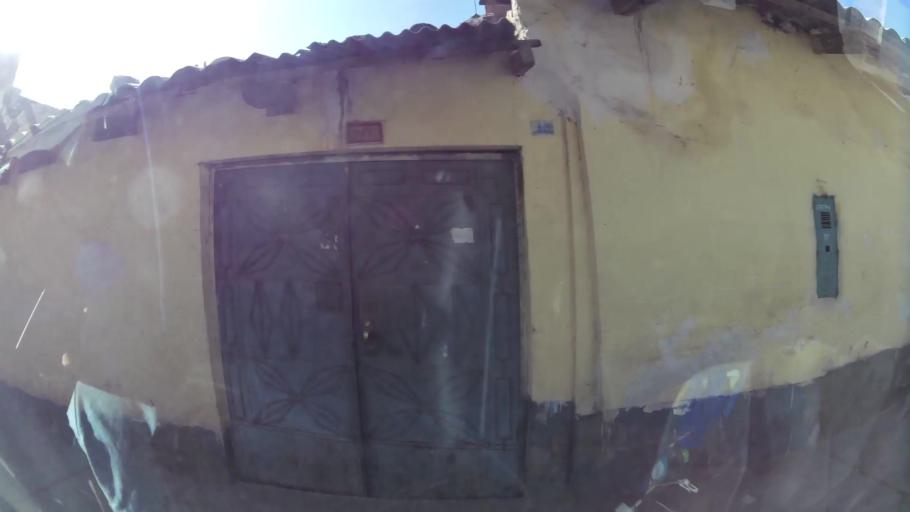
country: PE
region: Ayacucho
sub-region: Provincia de Huamanga
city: Ayacucho
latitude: -13.1637
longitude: -74.2314
